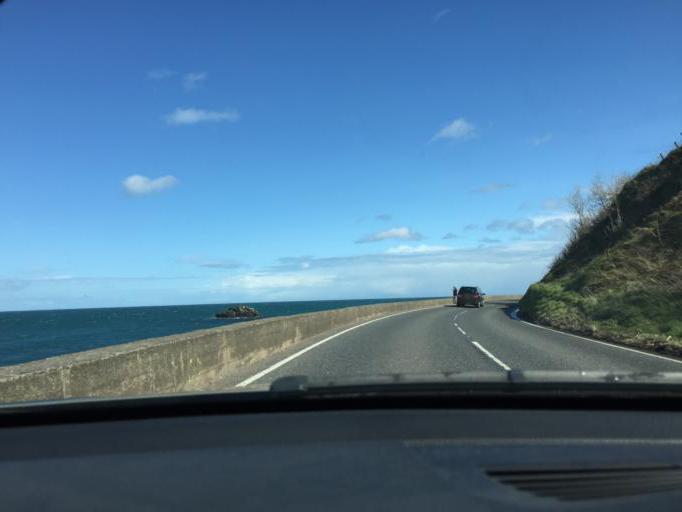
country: GB
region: Northern Ireland
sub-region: Larne District
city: Carnlough
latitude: 54.9809
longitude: -5.9713
